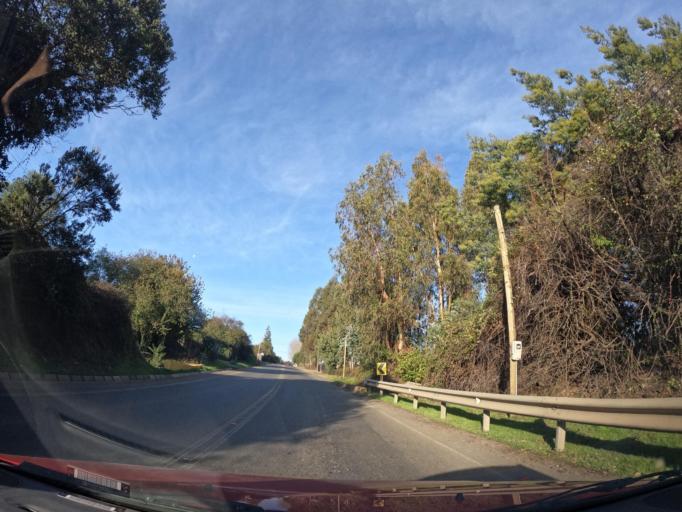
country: CL
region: Maule
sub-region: Provincia de Linares
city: Colbun
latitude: -35.5725
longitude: -71.3358
